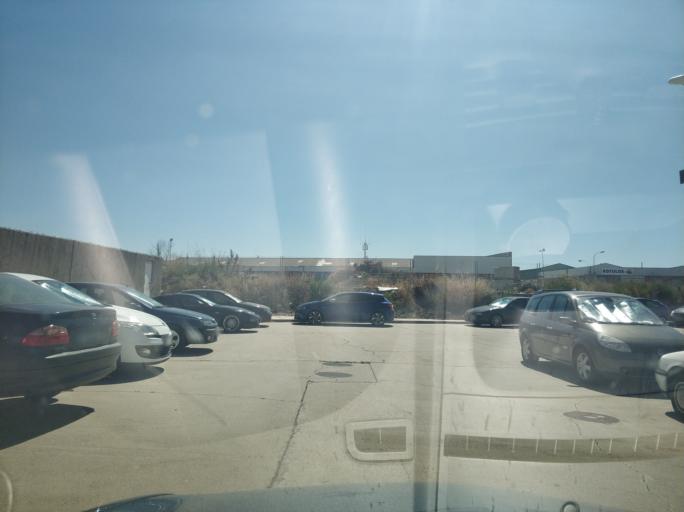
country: ES
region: Castille and Leon
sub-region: Provincia de Salamanca
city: Villares de la Reina
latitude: 40.9946
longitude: -5.6392
